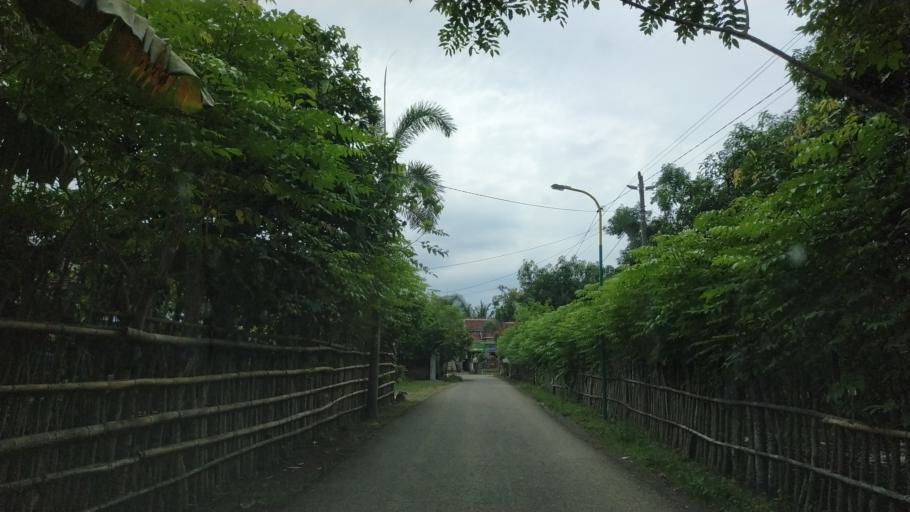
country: ID
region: Central Java
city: Krajan Tegalombo
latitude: -6.4239
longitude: 110.9847
